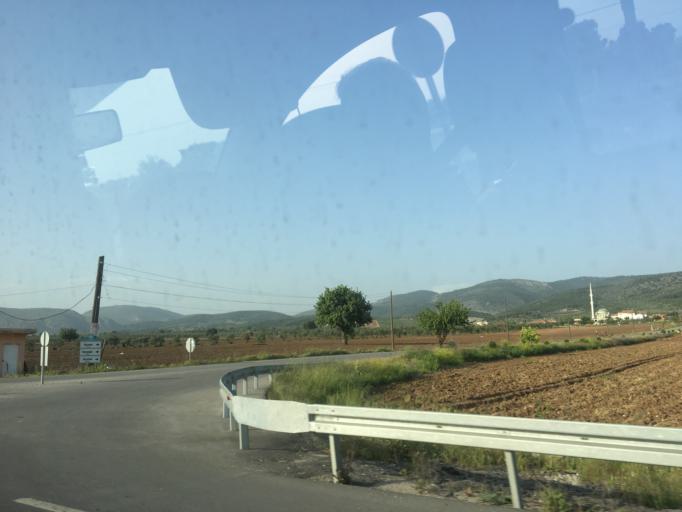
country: TR
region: Manisa
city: Golmarmara
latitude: 38.7913
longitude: 27.9007
